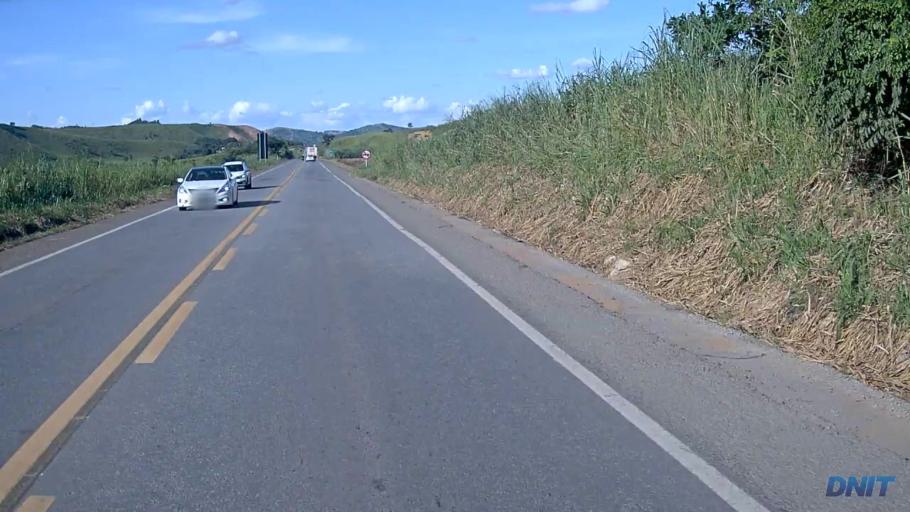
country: BR
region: Minas Gerais
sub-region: Belo Oriente
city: Belo Oriente
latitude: -19.1961
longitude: -42.2819
